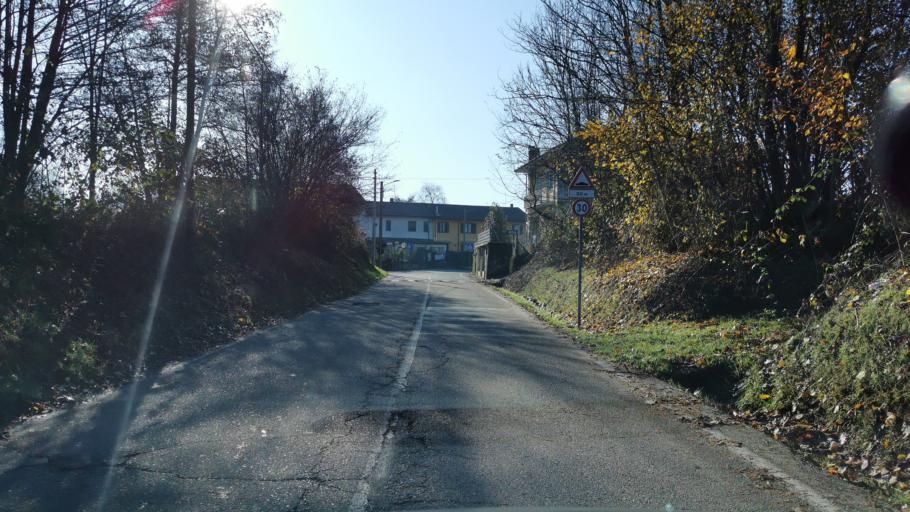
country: IT
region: Piedmont
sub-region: Provincia di Torino
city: Fiano
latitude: 45.2052
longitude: 7.5272
